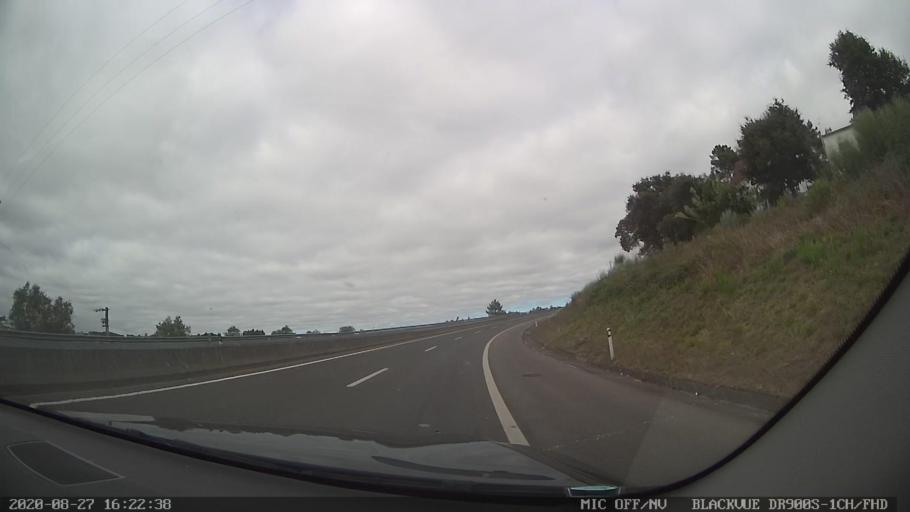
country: PT
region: Leiria
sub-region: Leiria
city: Leiria
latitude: 39.7488
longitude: -8.7800
